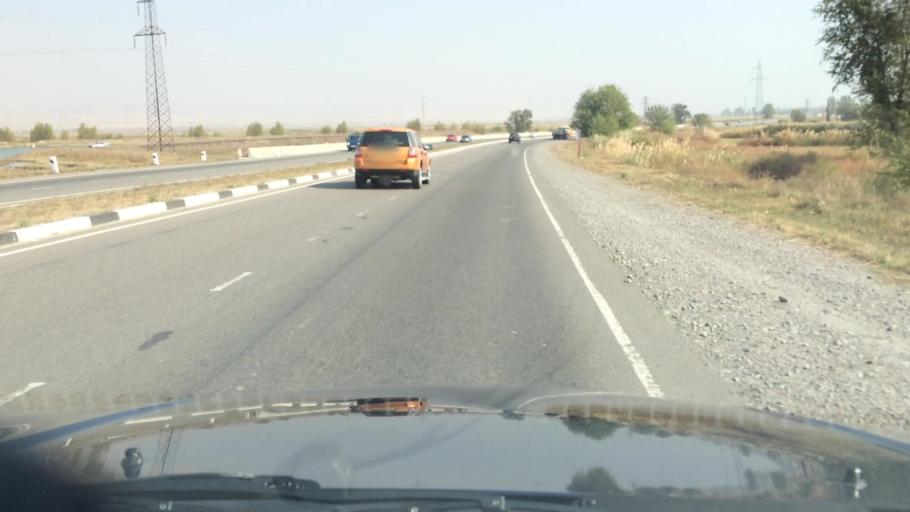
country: KG
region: Chuy
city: Kant
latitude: 42.9632
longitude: 74.8069
